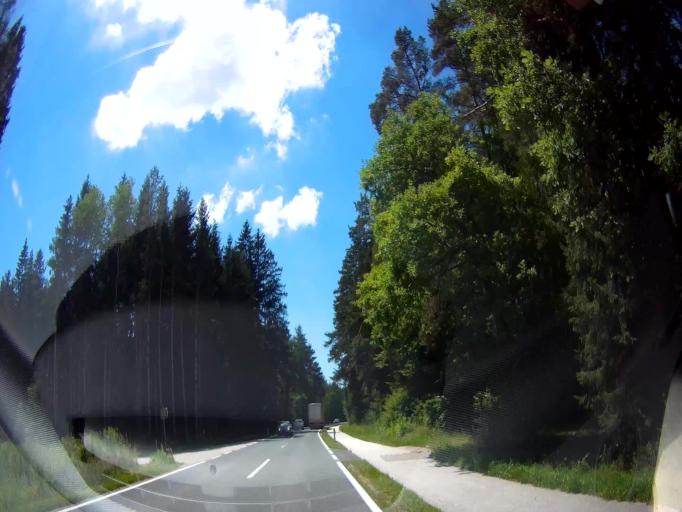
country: AT
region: Carinthia
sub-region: Politischer Bezirk Volkermarkt
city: Globasnitz
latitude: 46.6071
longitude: 14.6979
